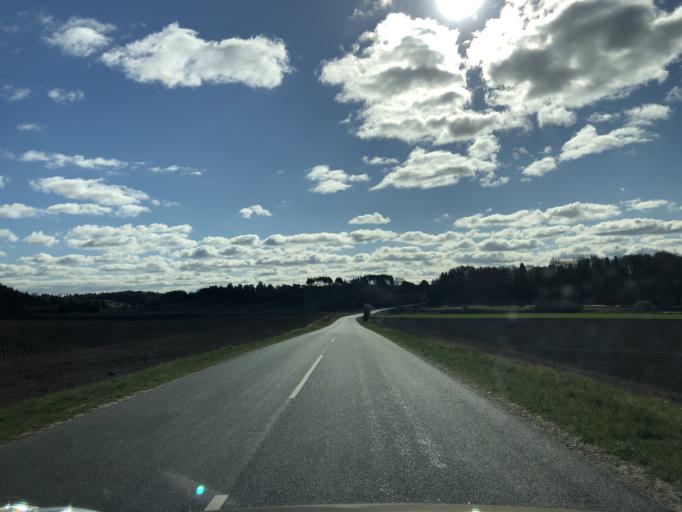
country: DK
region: North Denmark
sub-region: Vesthimmerland Kommune
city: Alestrup
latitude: 56.6123
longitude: 9.5314
